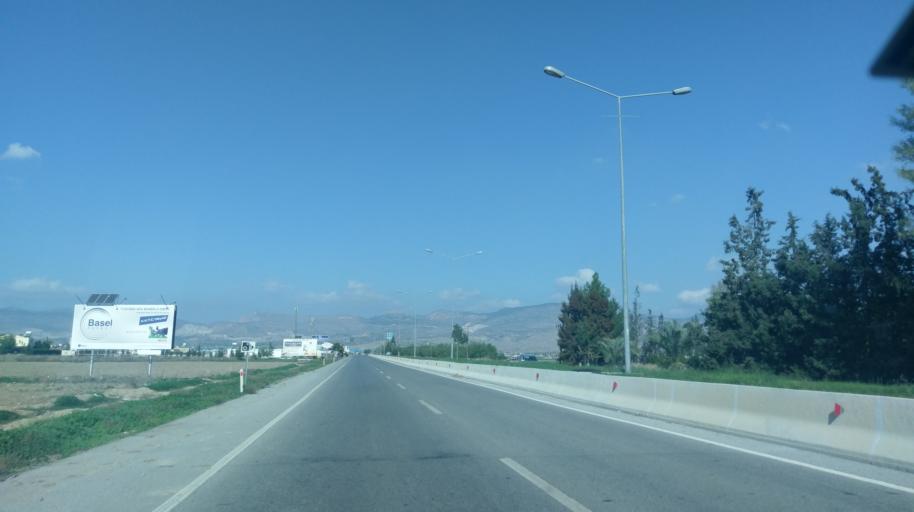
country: CY
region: Lefkosia
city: Geri
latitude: 35.2043
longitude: 33.4994
